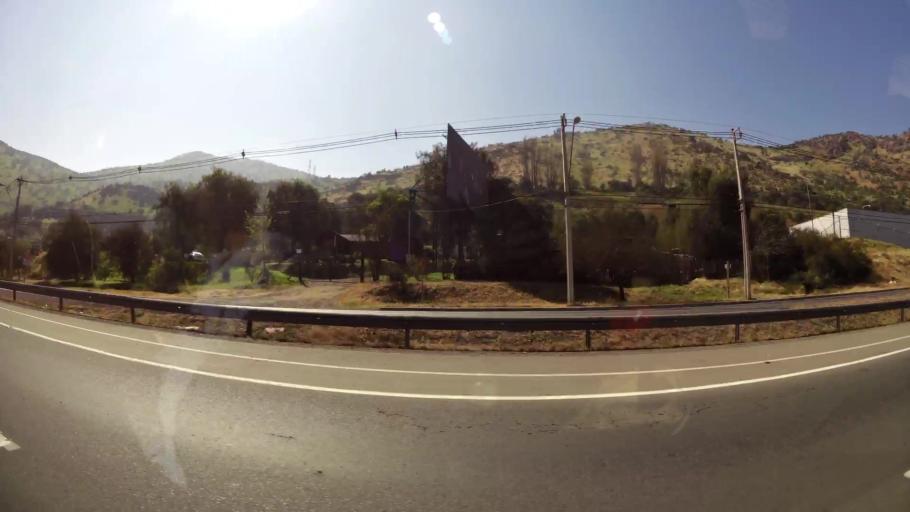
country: CL
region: Santiago Metropolitan
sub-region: Provincia de Chacabuco
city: Chicureo Abajo
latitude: -33.3379
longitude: -70.6924
